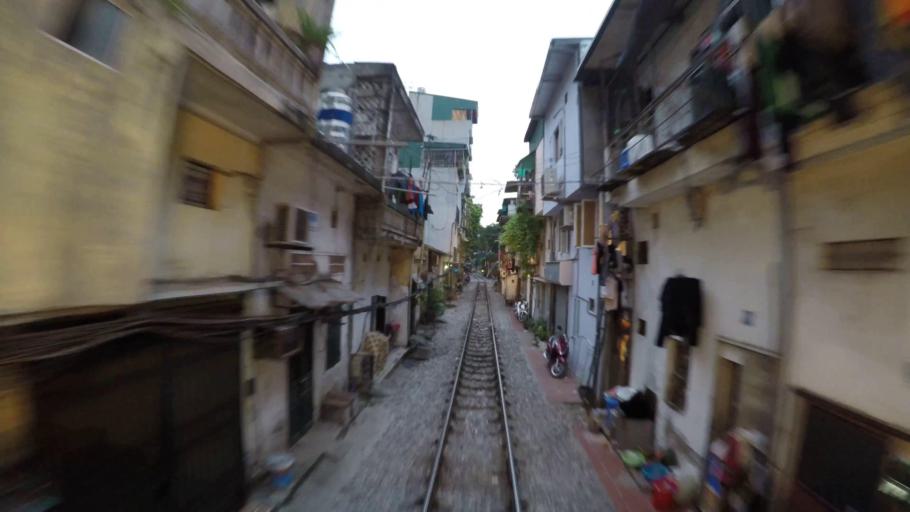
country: VN
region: Ha Noi
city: Hoan Kiem
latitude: 21.0384
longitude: 105.8466
